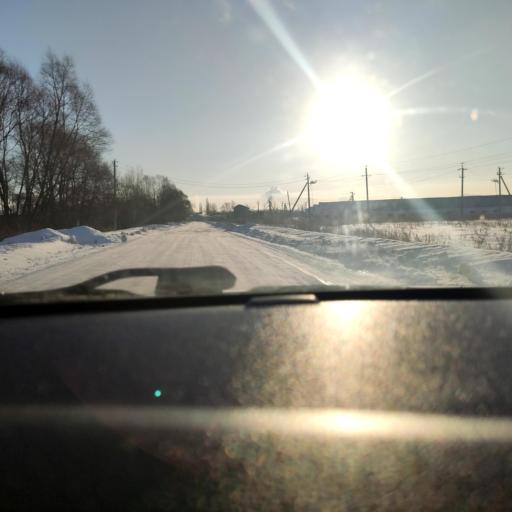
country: RU
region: Bashkortostan
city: Mikhaylovka
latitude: 54.7737
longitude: 55.8243
